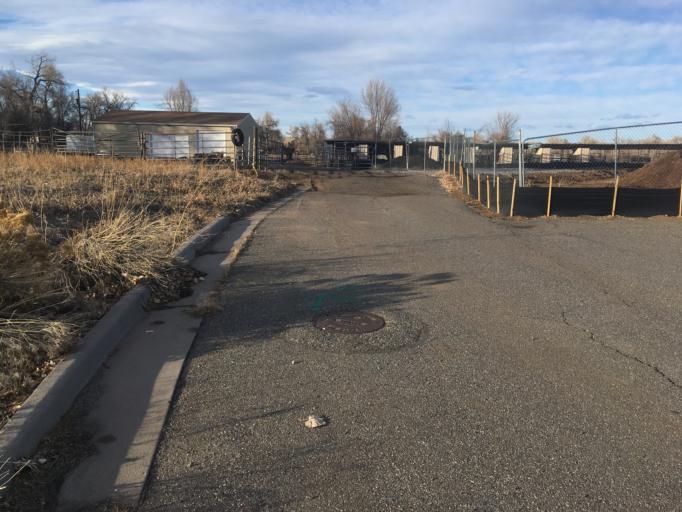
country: US
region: Colorado
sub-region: Jefferson County
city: Applewood
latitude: 39.8170
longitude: -105.1631
